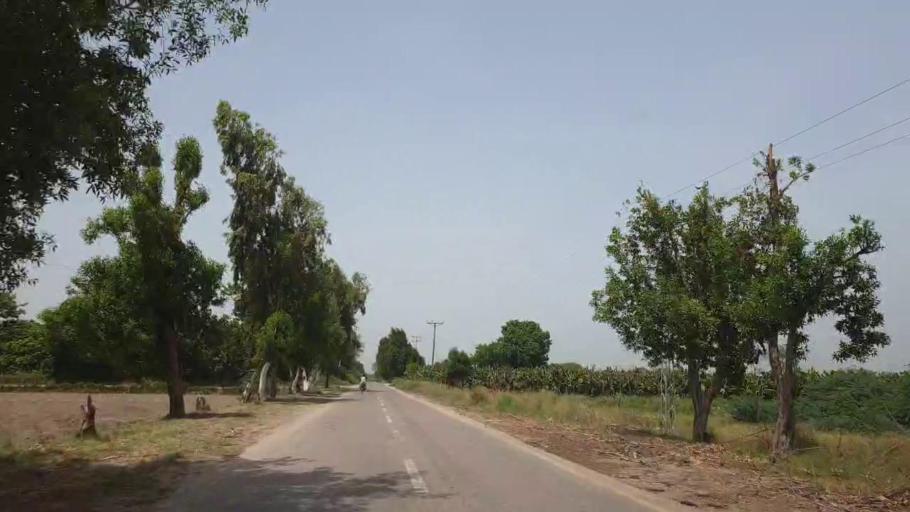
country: PK
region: Sindh
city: Sakrand
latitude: 26.1901
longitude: 68.2348
